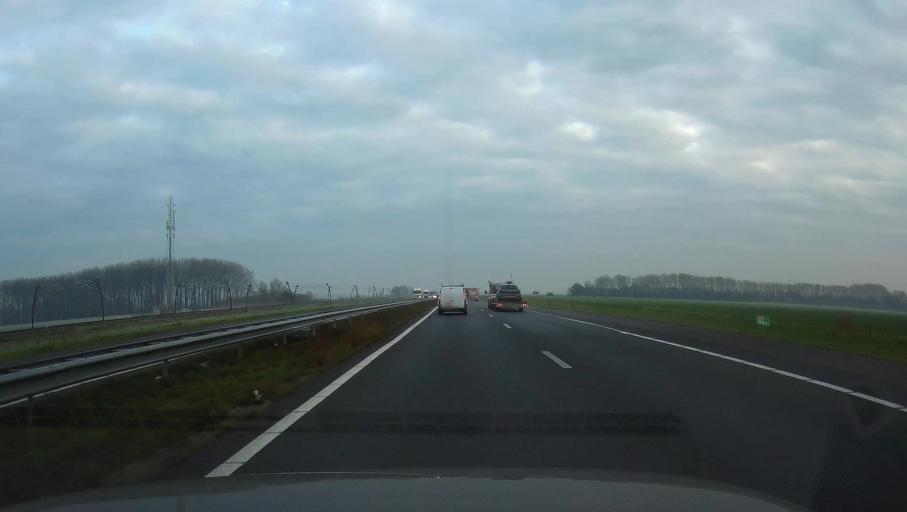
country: NL
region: South Holland
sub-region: Gemeente Leerdam
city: Leerdam
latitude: 51.8471
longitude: 5.1445
